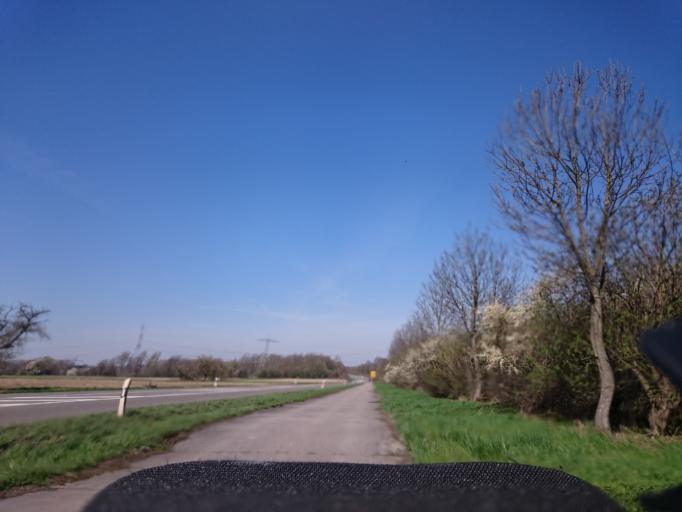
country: DE
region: Rheinland-Pfalz
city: Worth am Rhein
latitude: 49.0661
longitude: 8.2886
